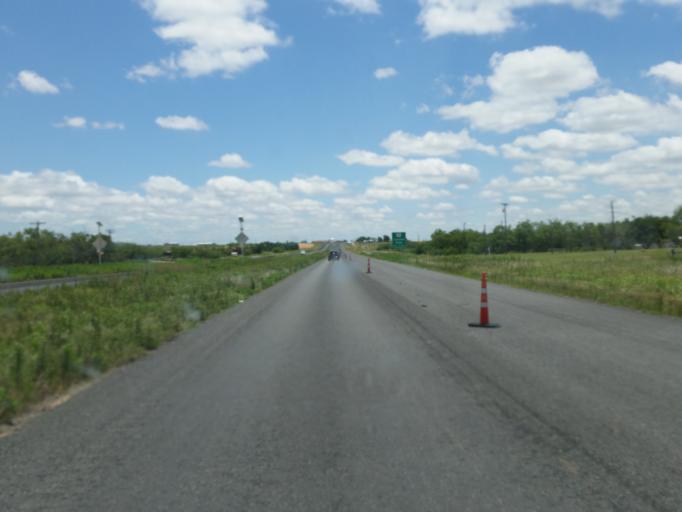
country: US
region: Texas
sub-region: Scurry County
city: Snyder
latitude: 32.7202
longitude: -100.8834
